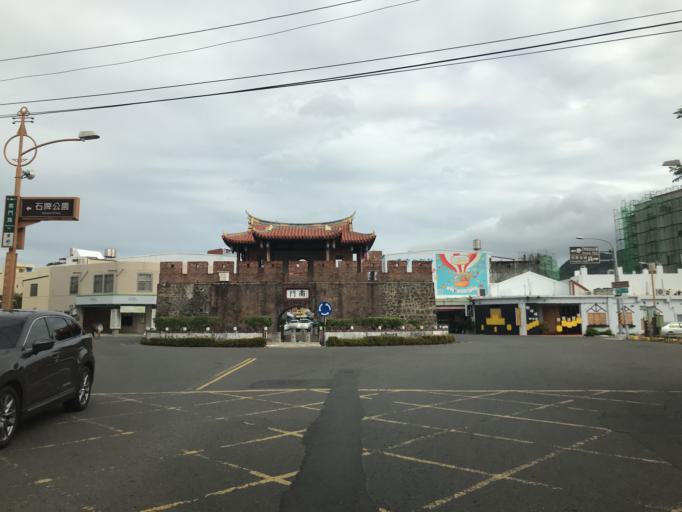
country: TW
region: Taiwan
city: Hengchun
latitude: 22.0002
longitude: 120.7447
